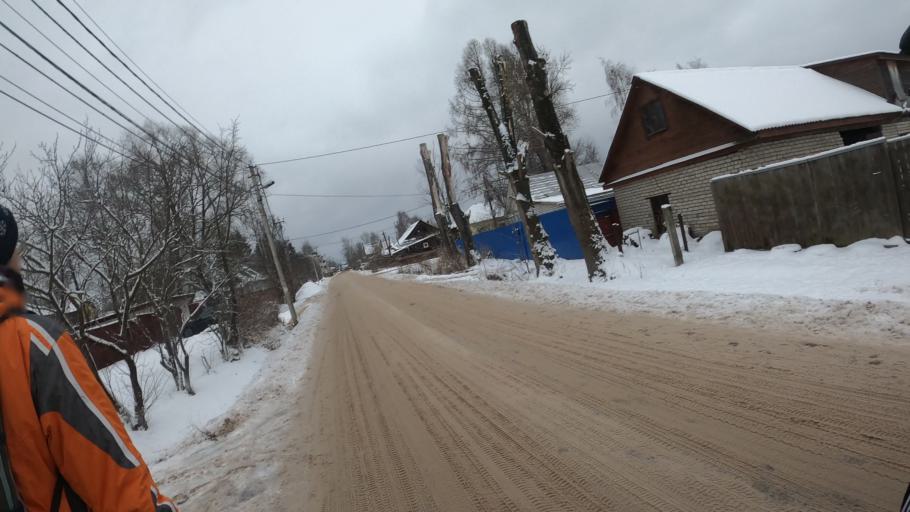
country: RU
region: Jaroslavl
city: Pereslavl'-Zalesskiy
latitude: 56.7287
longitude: 38.8377
